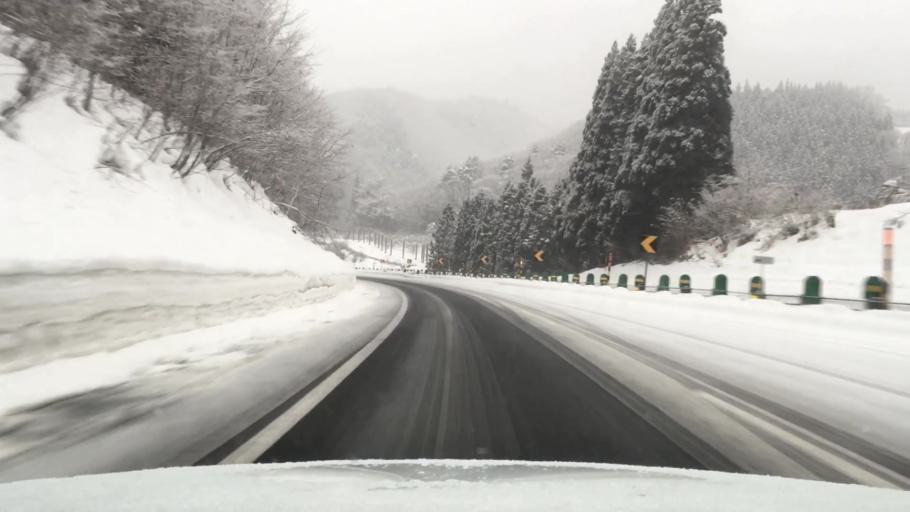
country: JP
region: Aomori
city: Kuroishi
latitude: 40.5224
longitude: 140.5992
